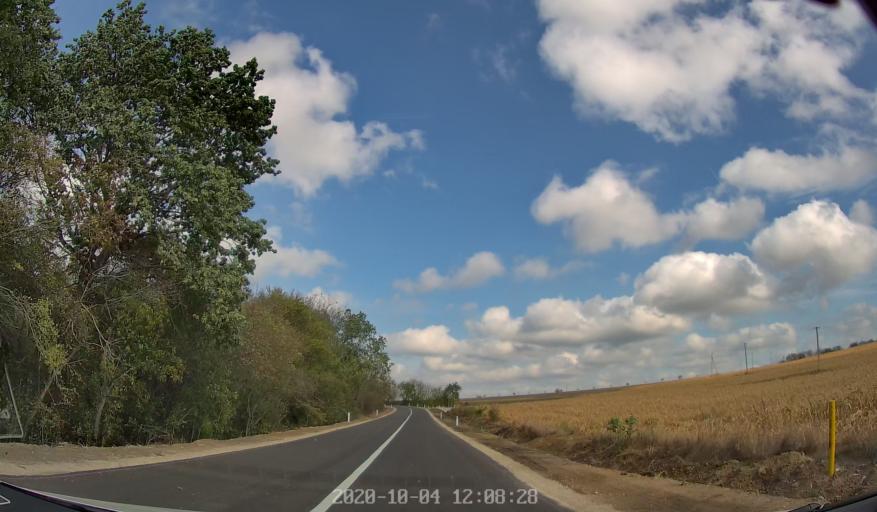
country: MD
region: Rezina
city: Saharna
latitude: 47.5949
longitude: 28.9767
